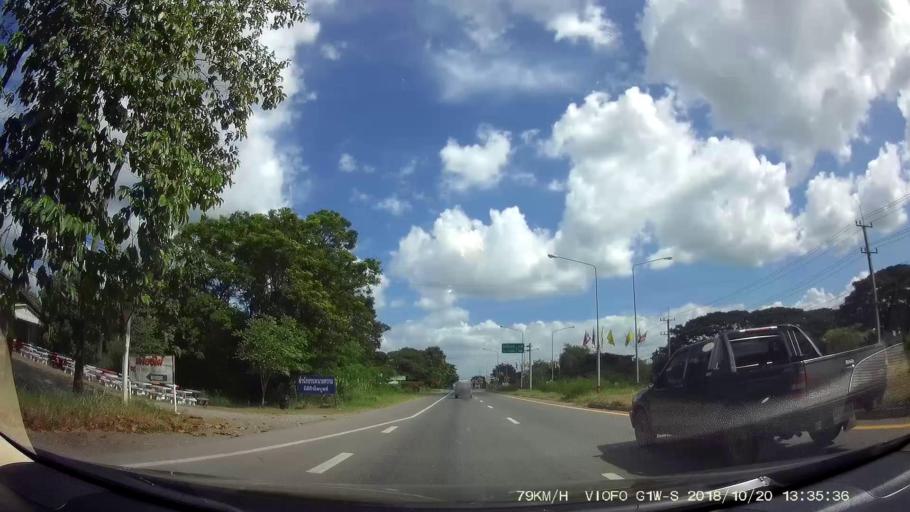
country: TH
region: Khon Kaen
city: Chum Phae
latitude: 16.5678
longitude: 102.0483
